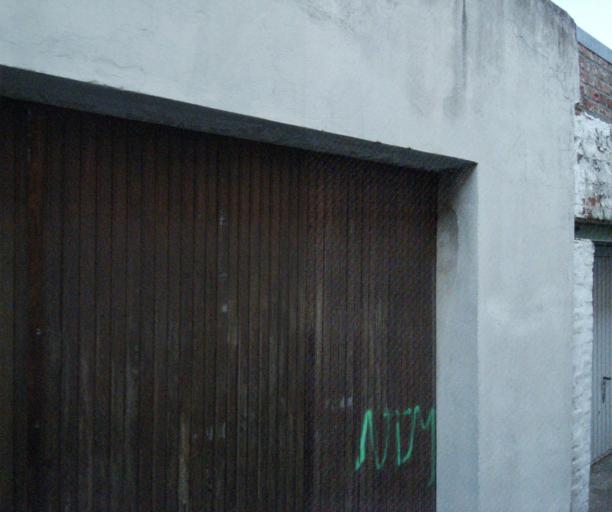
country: FR
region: Nord-Pas-de-Calais
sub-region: Departement du Nord
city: Mons-en-Baroeul
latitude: 50.6268
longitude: 3.1125
